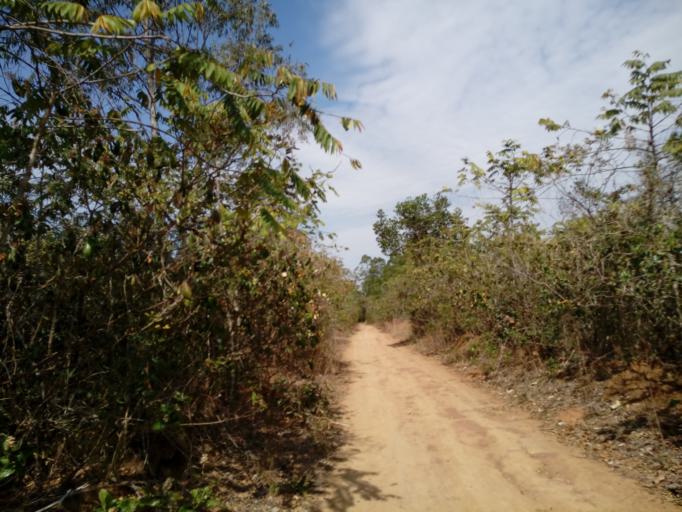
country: BR
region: Sao Paulo
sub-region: Sao Carlos
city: Sao Carlos
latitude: -21.9736
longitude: -47.8825
